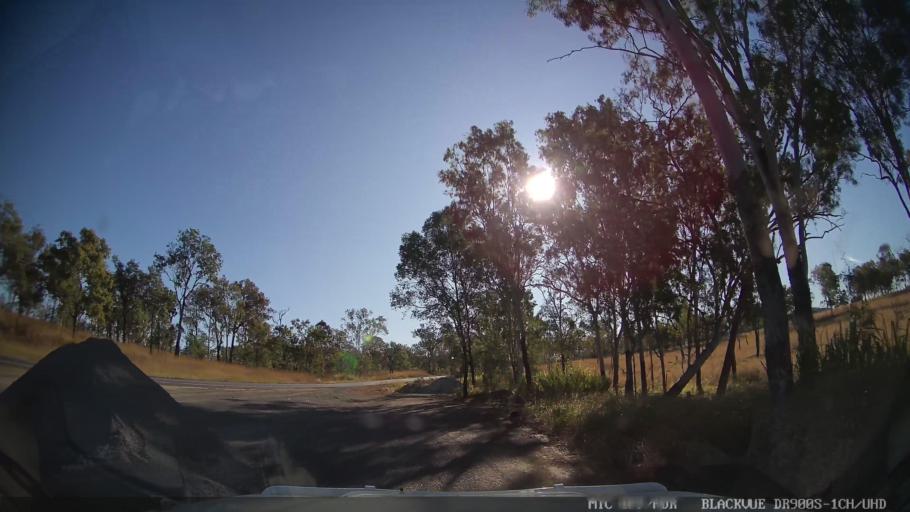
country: AU
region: Queensland
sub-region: Bundaberg
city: Sharon
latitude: -24.8781
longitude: 151.7433
